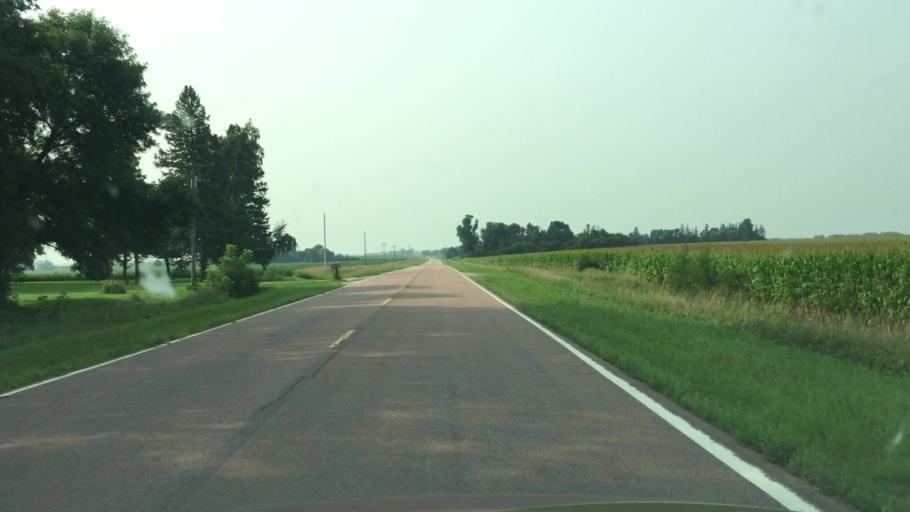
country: US
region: Iowa
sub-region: O'Brien County
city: Sheldon
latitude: 43.2532
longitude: -95.7832
